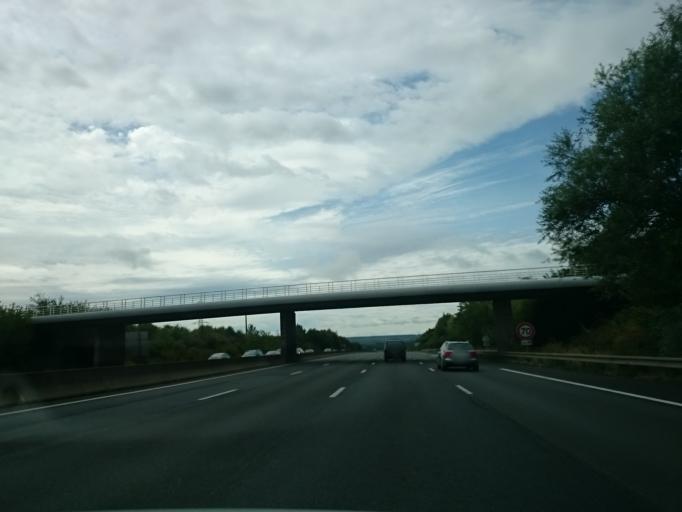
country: FR
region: Ile-de-France
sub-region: Departement de l'Essonne
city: Fontenay-les-Briis
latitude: 48.6304
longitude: 2.1424
